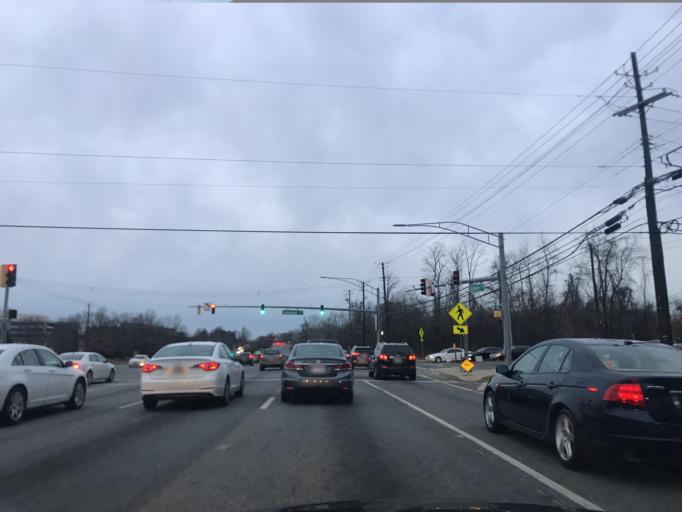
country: US
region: Maryland
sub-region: Prince George's County
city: Lake Arbor
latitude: 38.9125
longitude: -76.8381
